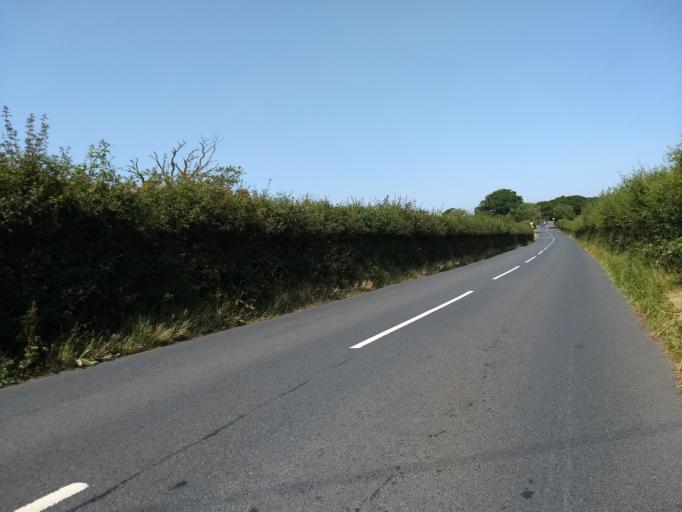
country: GB
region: England
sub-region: Isle of Wight
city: Northwood
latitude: 50.7234
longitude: -1.3534
